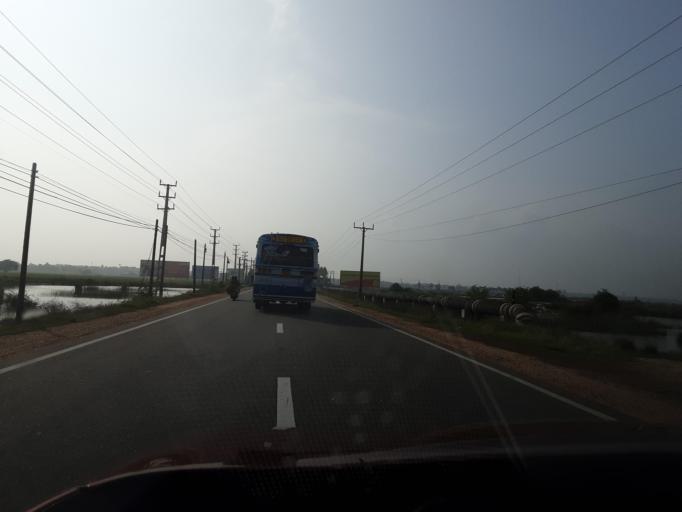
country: LK
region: Northern Province
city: Jaffna
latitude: 9.6631
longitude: 80.0655
